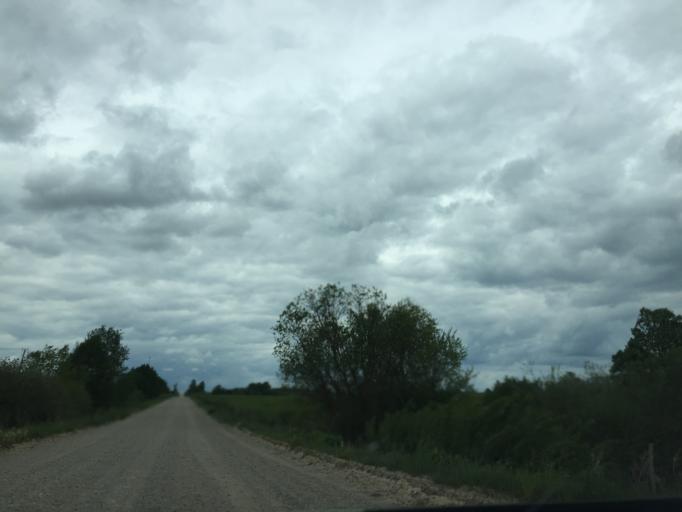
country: LV
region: Dagda
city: Dagda
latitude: 56.0057
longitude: 27.6052
